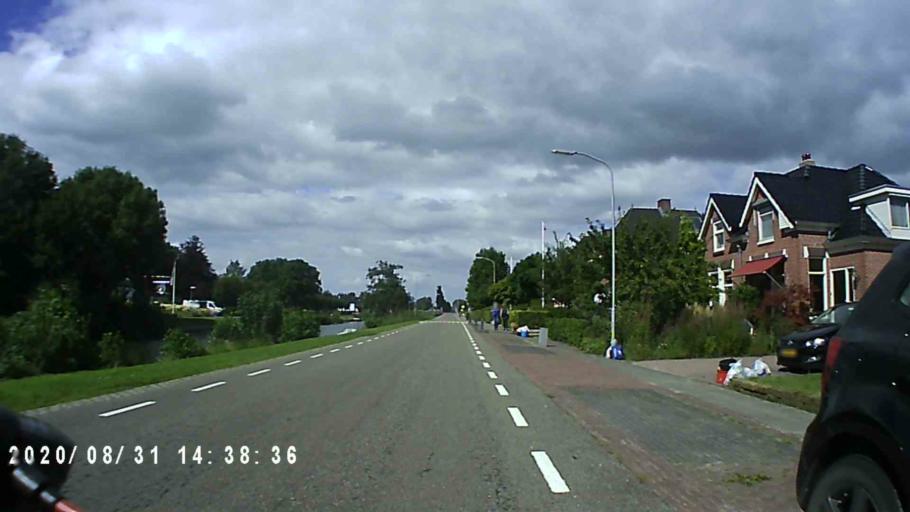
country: NL
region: Groningen
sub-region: Gemeente Zuidhorn
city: Zuidhorn
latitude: 53.2405
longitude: 6.3907
